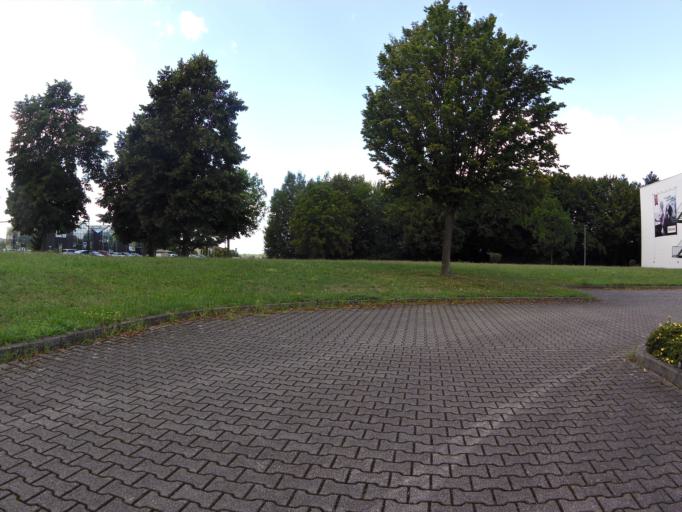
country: DE
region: Baden-Wuerttemberg
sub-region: Freiburg Region
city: Lahr
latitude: 48.3489
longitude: 7.8227
